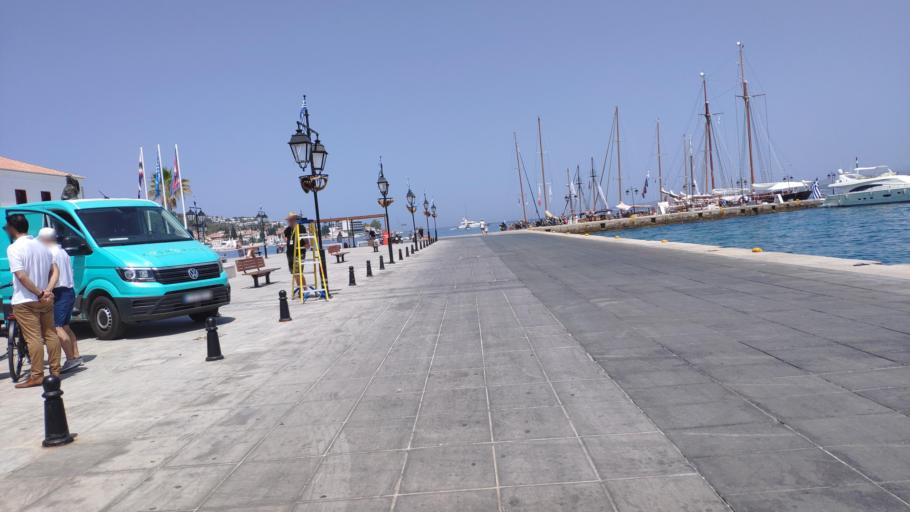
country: GR
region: Attica
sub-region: Nomos Piraios
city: Spetses
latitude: 37.2688
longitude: 23.1553
